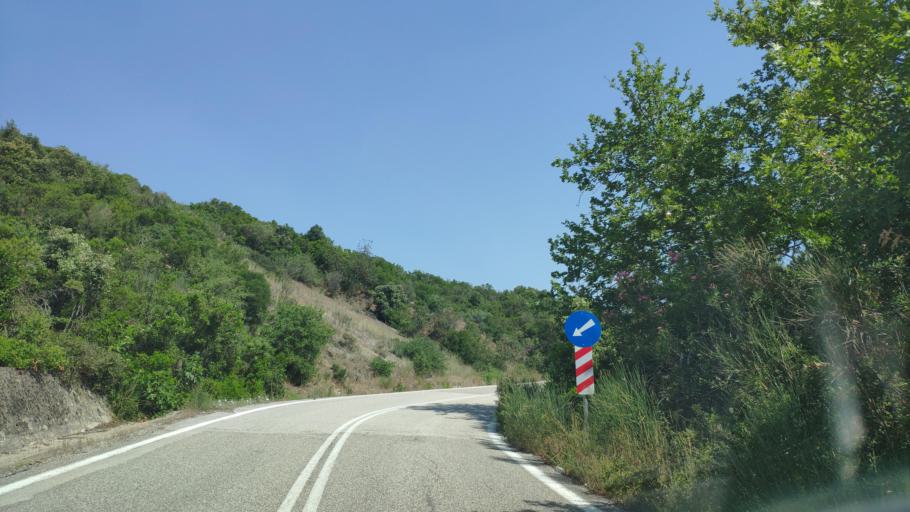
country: GR
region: West Greece
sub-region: Nomos Aitolias kai Akarnanias
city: Lepenou
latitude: 38.7665
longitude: 21.3371
